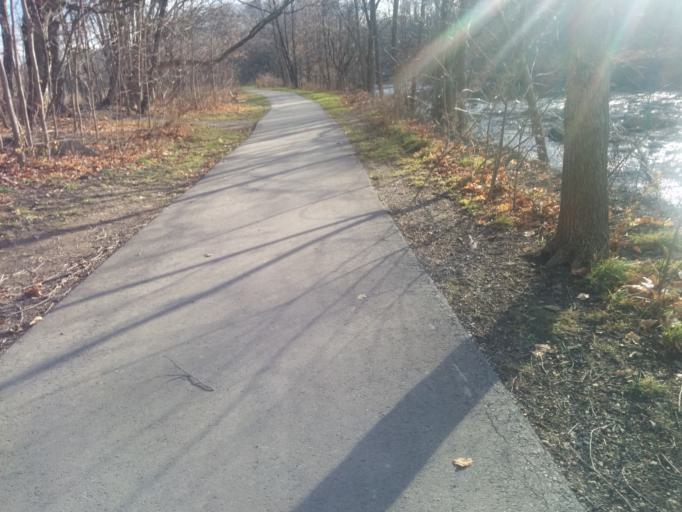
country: CA
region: Ontario
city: Etobicoke
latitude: 43.6015
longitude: -79.5559
